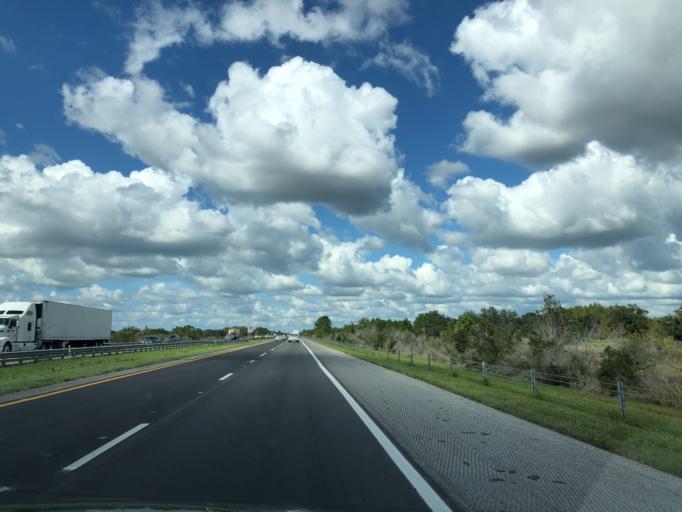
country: US
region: Florida
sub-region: Osceola County
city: Saint Cloud
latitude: 27.9369
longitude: -81.0723
